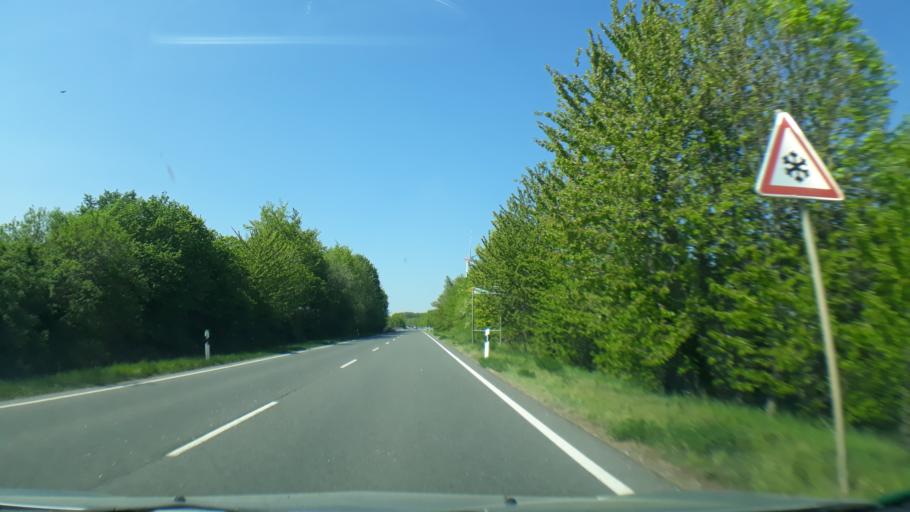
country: DE
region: North Rhine-Westphalia
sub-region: Regierungsbezirk Koln
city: Nideggen
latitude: 50.7024
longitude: 6.5185
